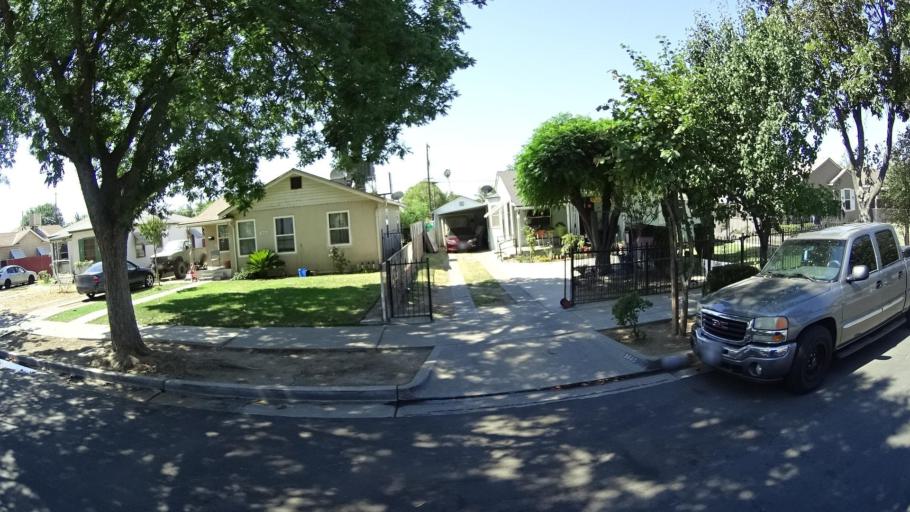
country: US
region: California
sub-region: Fresno County
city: Fresno
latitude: 36.7268
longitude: -119.7599
